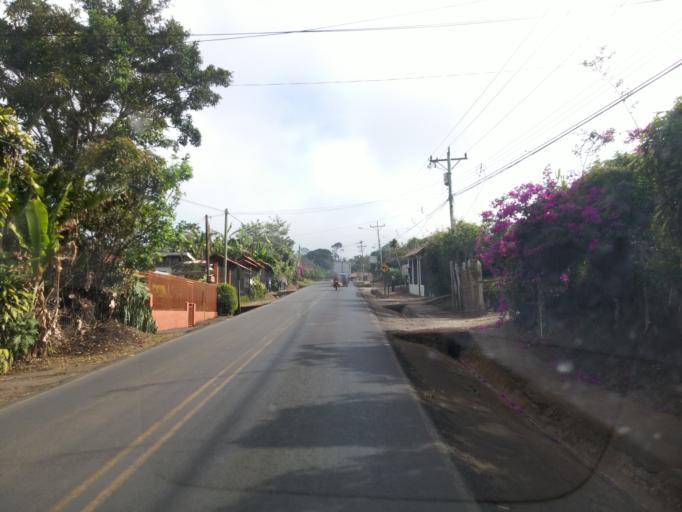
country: CR
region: Alajuela
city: San Ramon
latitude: 10.1127
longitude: -84.4691
